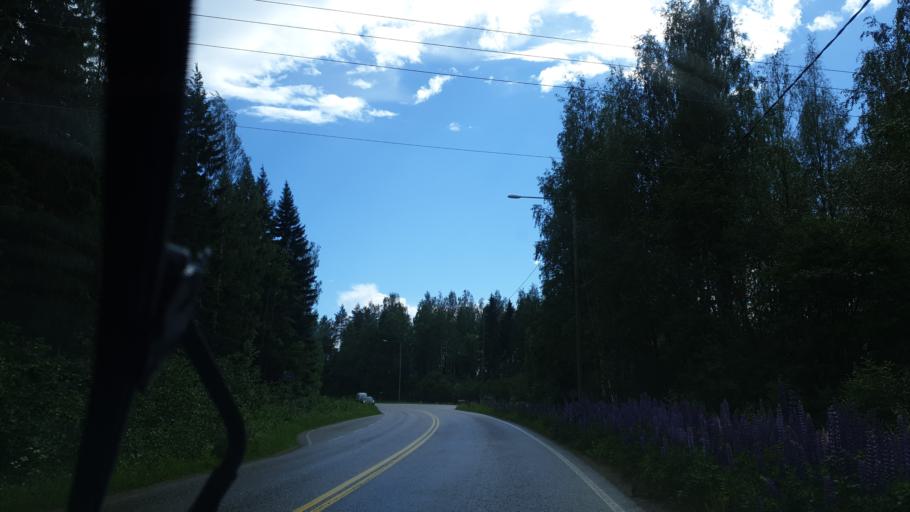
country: FI
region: Northern Savo
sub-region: Kuopio
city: Kuopio
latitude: 62.9059
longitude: 27.8442
